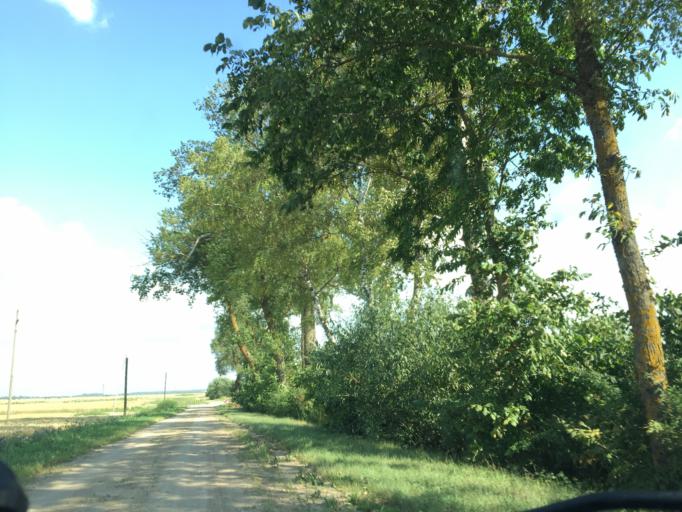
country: LV
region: Jelgava
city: Jelgava
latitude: 56.4710
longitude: 23.6999
